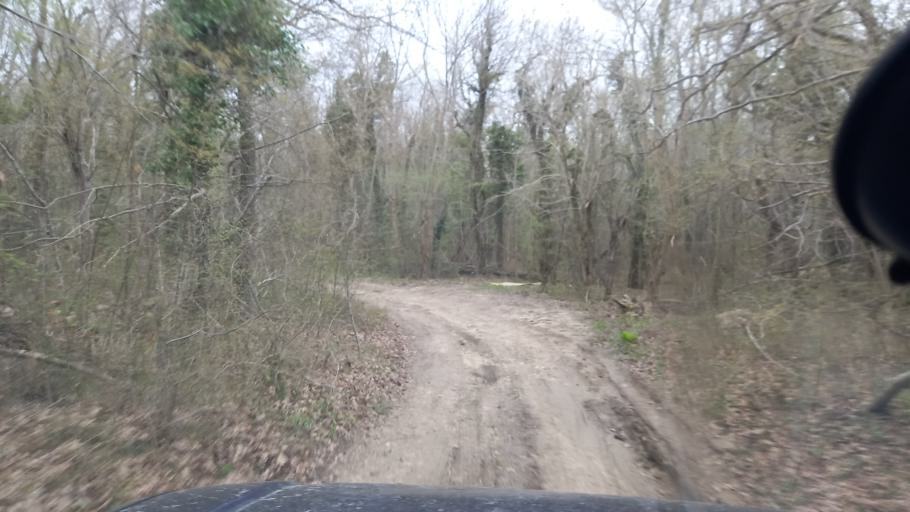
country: RU
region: Krasnodarskiy
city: Dzhubga
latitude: 44.3143
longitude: 38.6792
